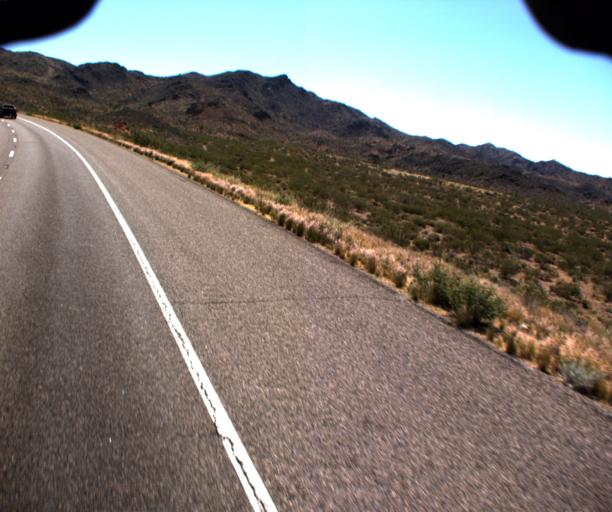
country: US
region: Arizona
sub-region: Mohave County
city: Bullhead City
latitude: 35.1941
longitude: -114.4103
